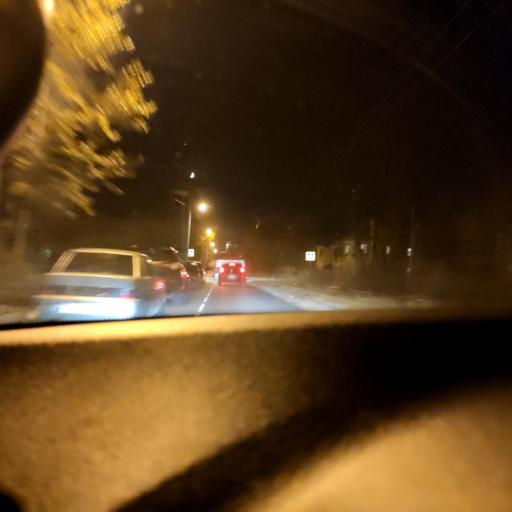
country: RU
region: Samara
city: Petra-Dubrava
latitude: 53.2321
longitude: 50.2853
